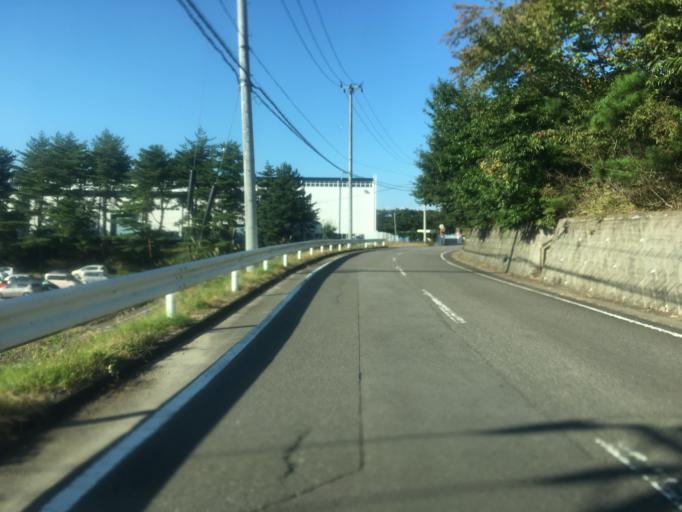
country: JP
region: Fukushima
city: Nihommatsu
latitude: 37.6578
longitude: 140.4863
